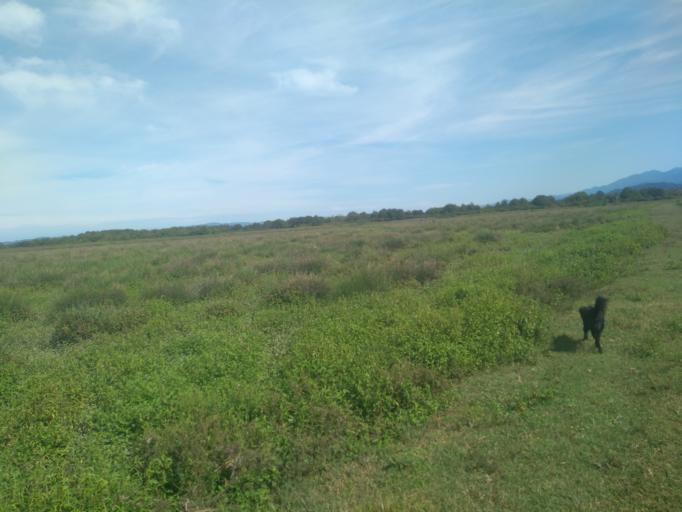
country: GE
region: Ajaria
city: Kobuleti
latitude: 41.8633
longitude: 41.7857
